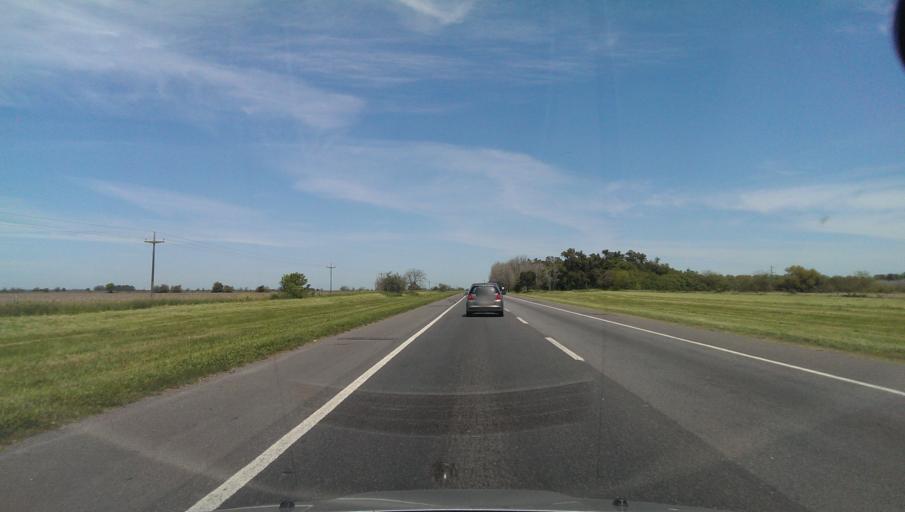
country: AR
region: Buenos Aires
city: San Miguel del Monte
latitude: -35.6203
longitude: -58.8338
